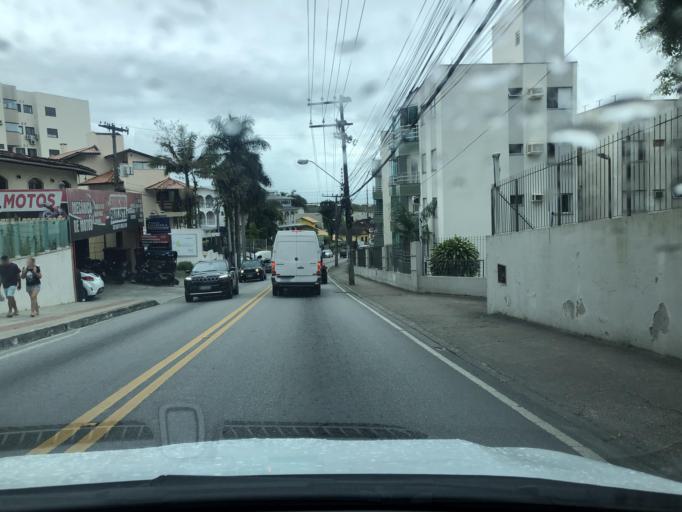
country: BR
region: Santa Catarina
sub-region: Florianopolis
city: Pantanal
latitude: -27.6124
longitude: -48.5255
